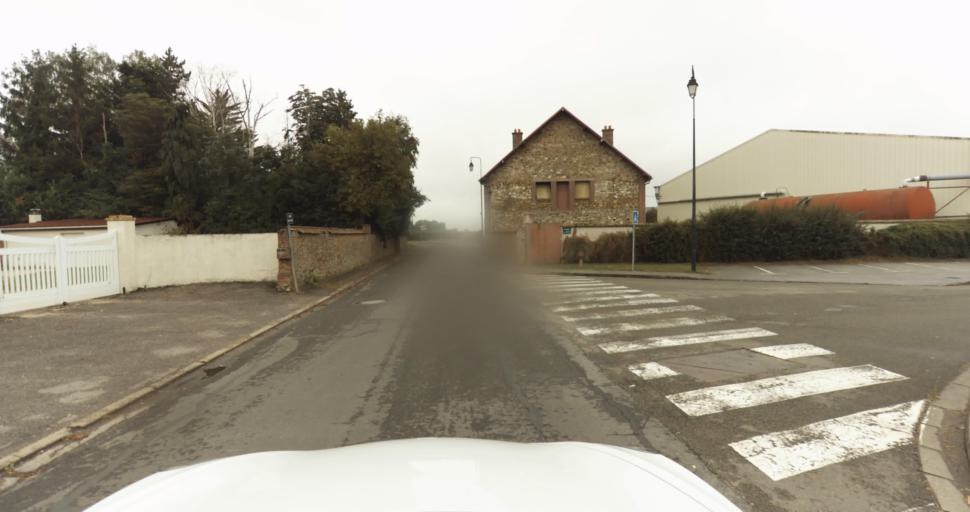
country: FR
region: Haute-Normandie
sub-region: Departement de l'Eure
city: Aviron
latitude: 49.0851
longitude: 1.0714
